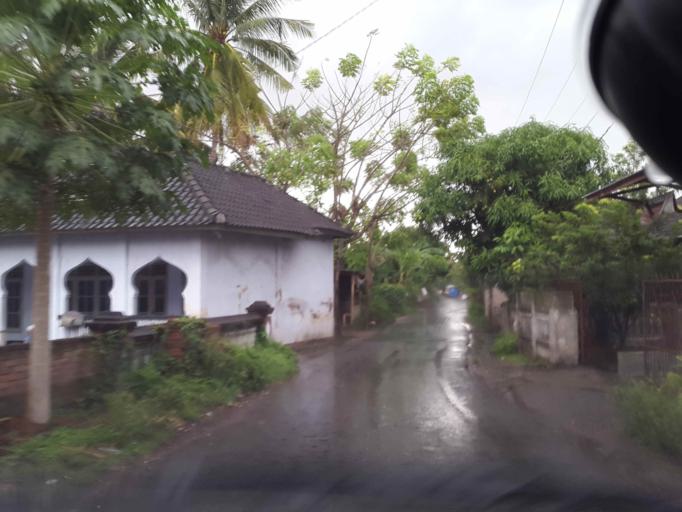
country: ID
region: West Nusa Tenggara
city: Kediri
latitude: -8.6592
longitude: 116.1307
